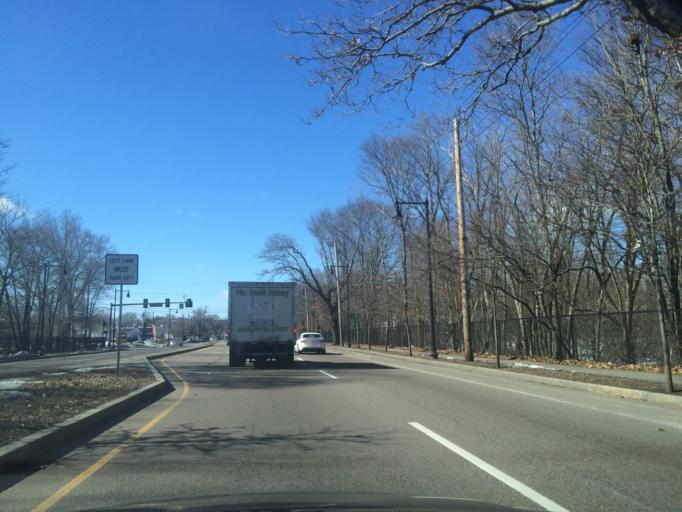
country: US
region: Massachusetts
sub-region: Suffolk County
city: Jamaica Plain
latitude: 42.2883
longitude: -71.1057
